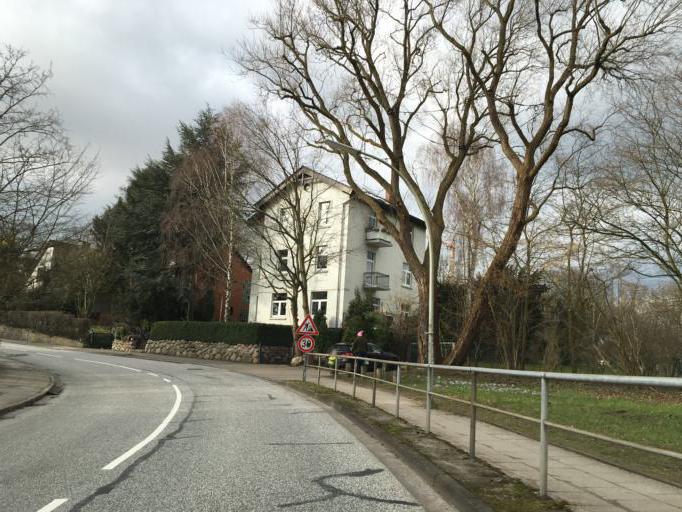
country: DE
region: Hamburg
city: Altona
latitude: 53.5549
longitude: 9.8730
